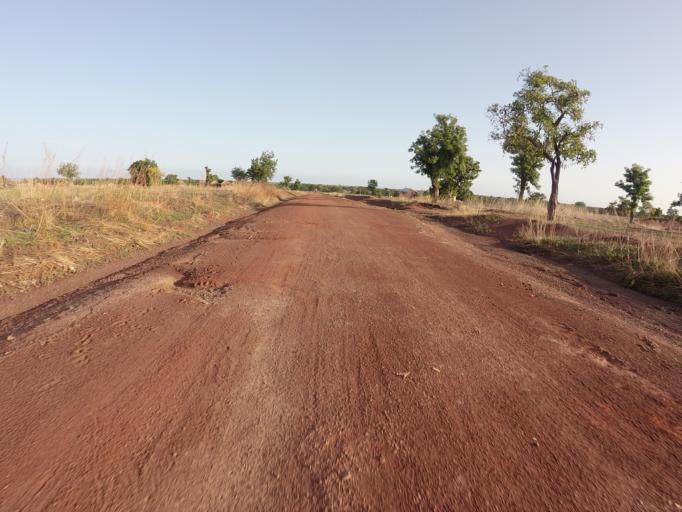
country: TG
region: Savanes
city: Sansanne-Mango
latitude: 10.3536
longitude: -0.0931
